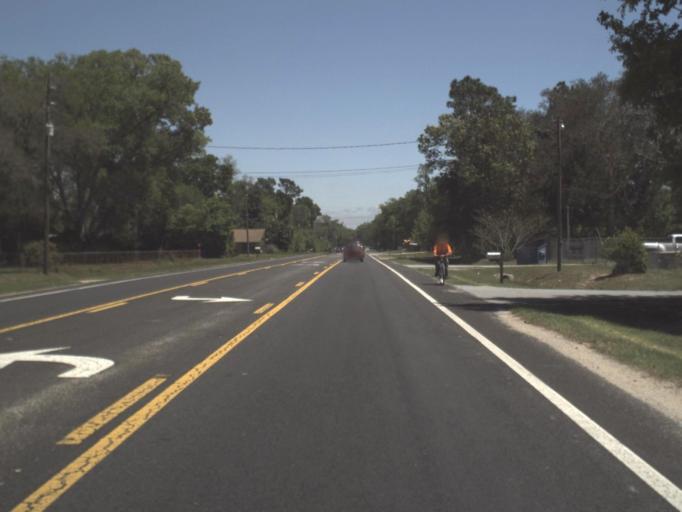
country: US
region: Florida
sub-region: Escambia County
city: Bellview
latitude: 30.4869
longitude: -87.3141
